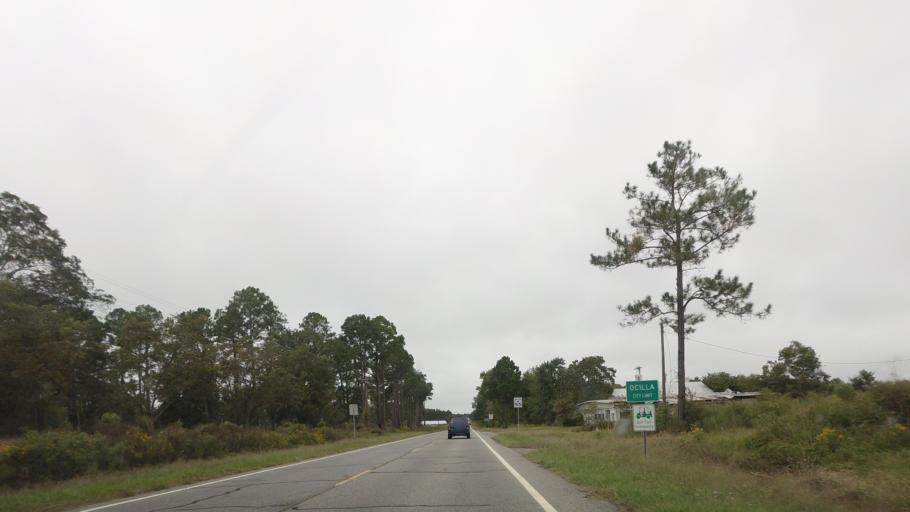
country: US
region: Georgia
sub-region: Irwin County
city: Ocilla
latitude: 31.5665
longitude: -83.2529
